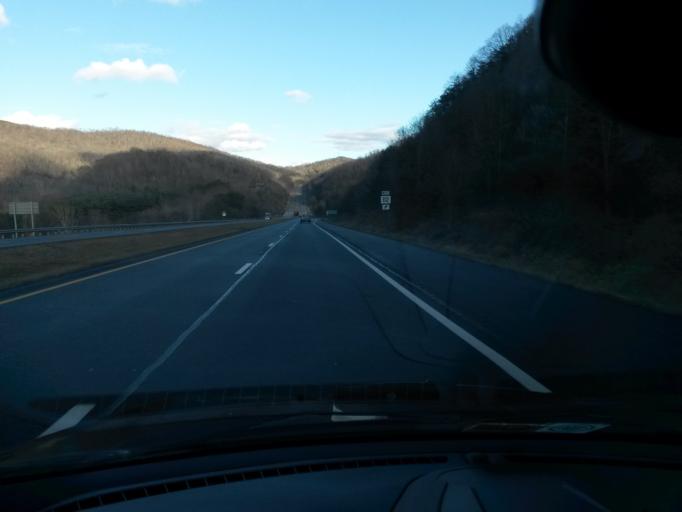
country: US
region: West Virginia
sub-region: Mercer County
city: Athens
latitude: 37.3408
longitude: -80.9641
